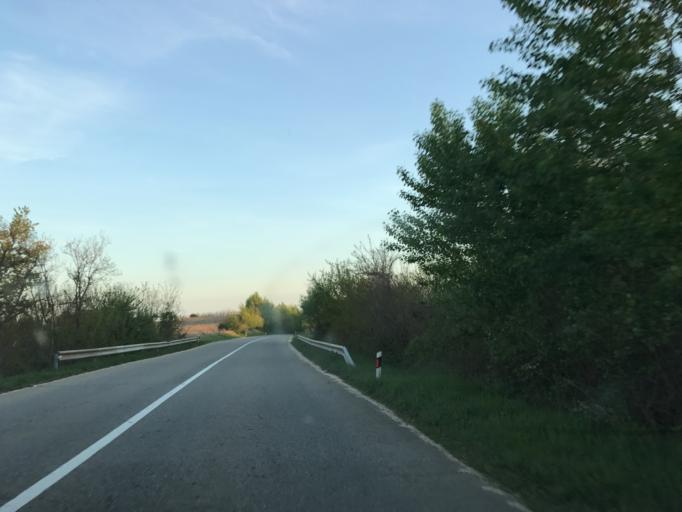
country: RO
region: Mehedinti
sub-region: Comuna Gogosu
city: Ostrovu Mare
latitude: 44.3766
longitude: 22.4801
